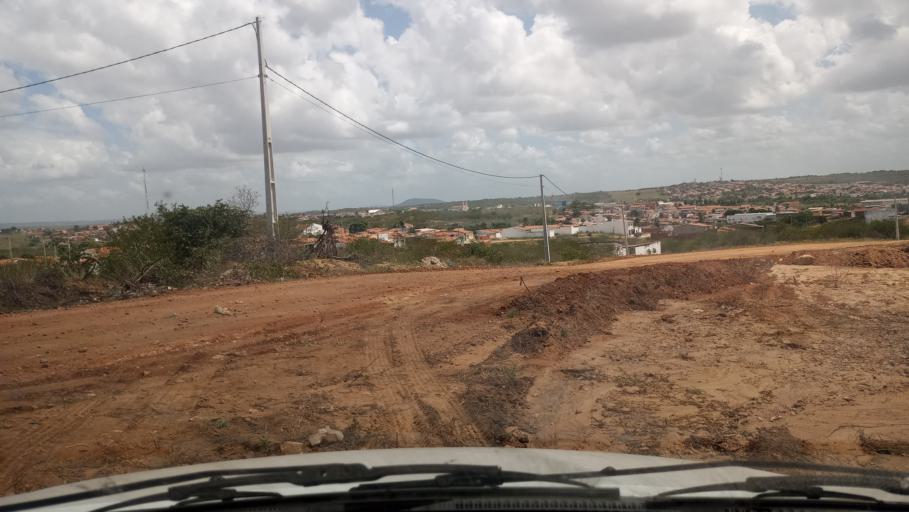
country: BR
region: Rio Grande do Norte
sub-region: Sao Paulo Do Potengi
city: Sao Paulo do Potengi
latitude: -5.9061
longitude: -35.7607
